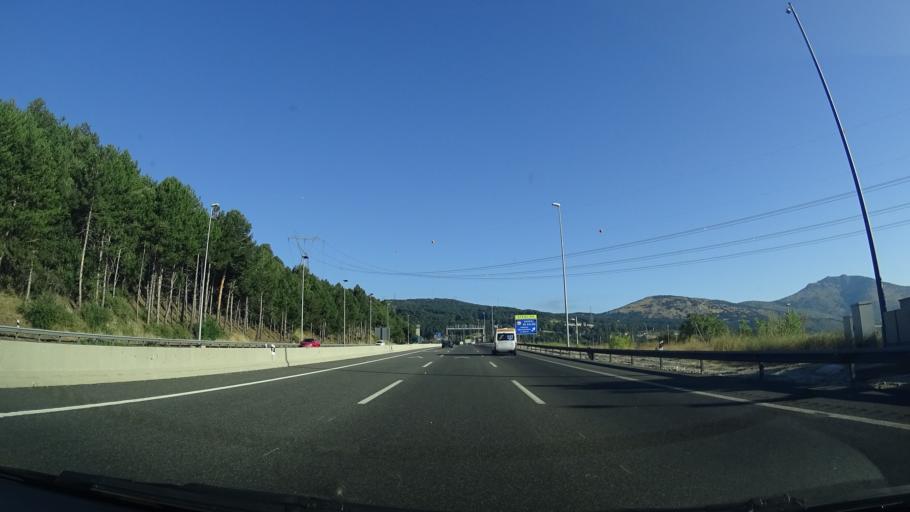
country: ES
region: Madrid
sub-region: Provincia de Madrid
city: Guadarrama
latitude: 40.6920
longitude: -4.1234
